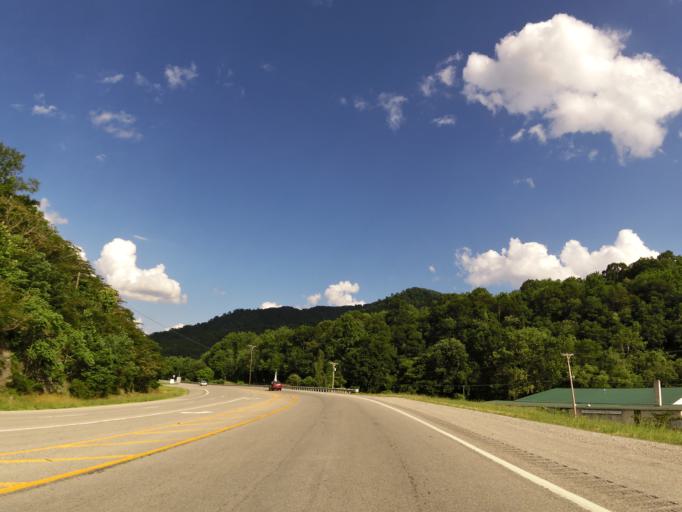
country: US
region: Kentucky
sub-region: Harlan County
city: Harlan
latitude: 36.8089
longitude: -83.3110
